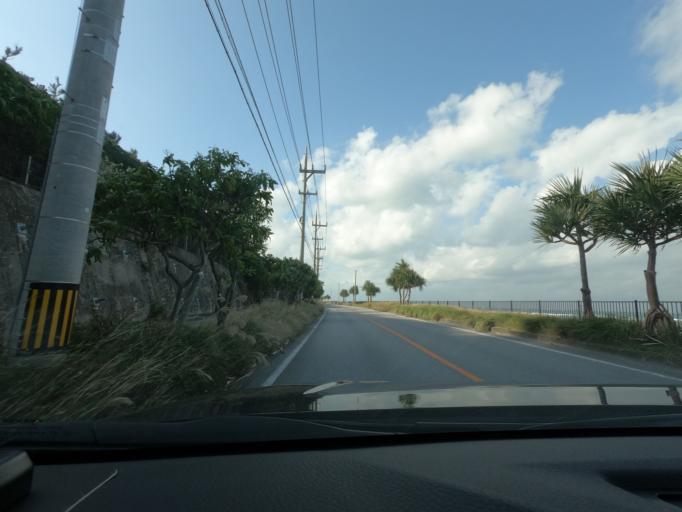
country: JP
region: Okinawa
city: Nago
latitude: 26.7635
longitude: 128.1939
